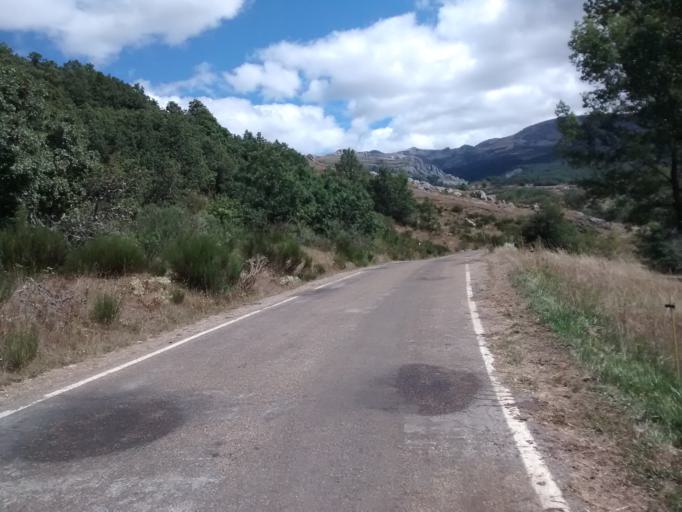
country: ES
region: Castille and Leon
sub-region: Provincia de Palencia
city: San Cebrian de Muda
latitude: 42.9464
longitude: -4.4437
